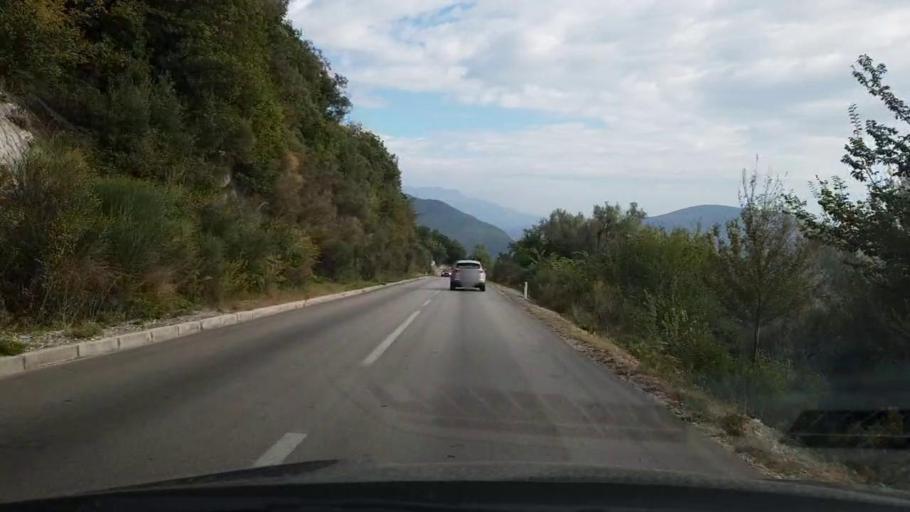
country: ME
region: Herceg Novi
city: Herceg-Novi
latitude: 42.4693
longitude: 18.5400
